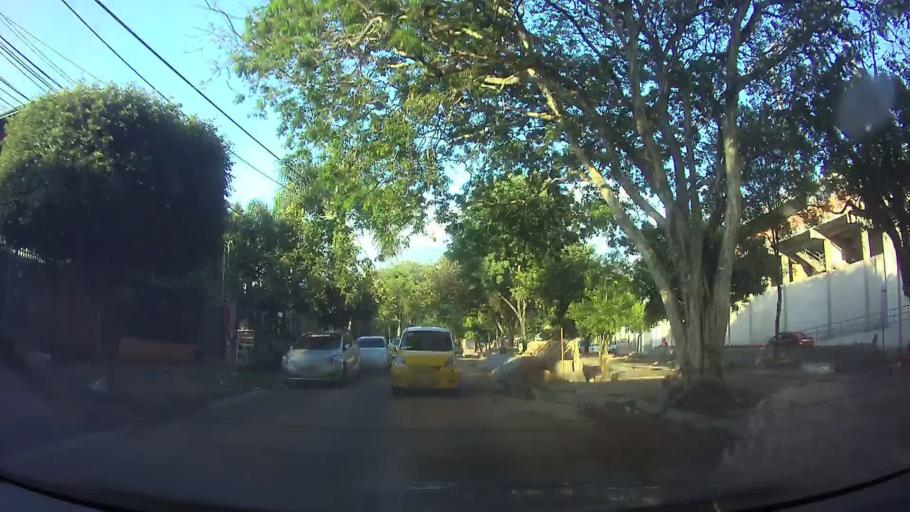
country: PY
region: Asuncion
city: Asuncion
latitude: -25.2980
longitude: -57.6407
